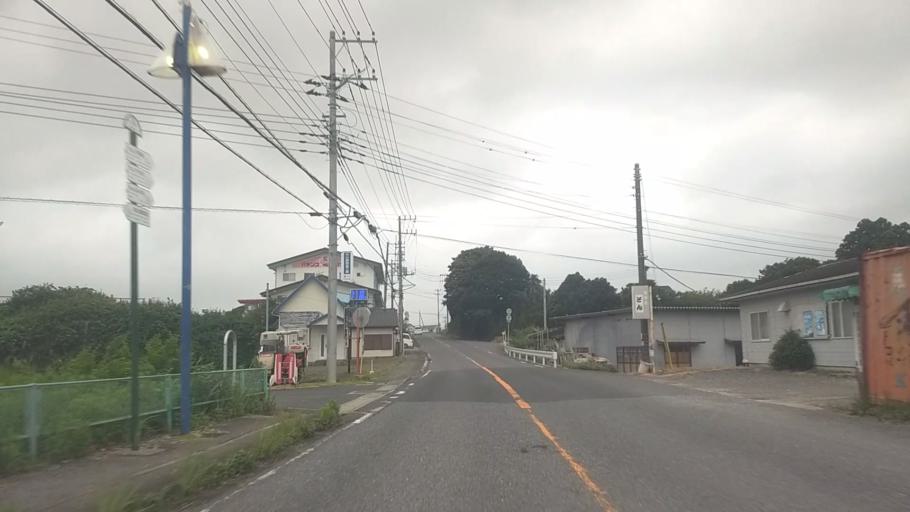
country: JP
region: Chiba
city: Kawaguchi
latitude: 35.1183
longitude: 140.0738
